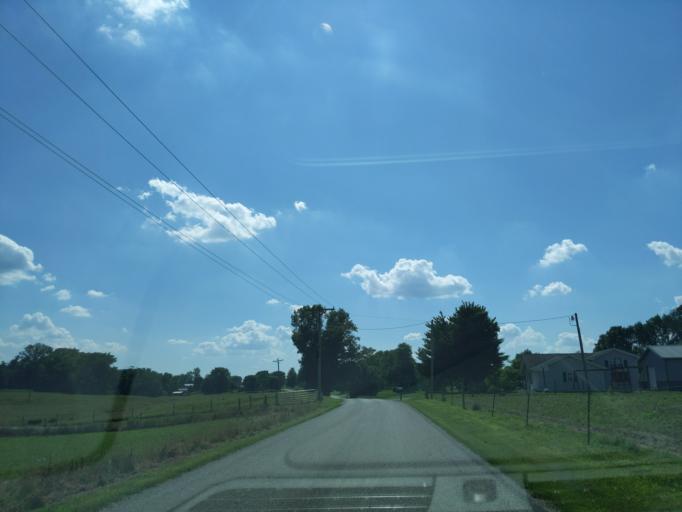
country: US
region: Indiana
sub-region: Ripley County
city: Osgood
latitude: 39.2007
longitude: -85.3747
